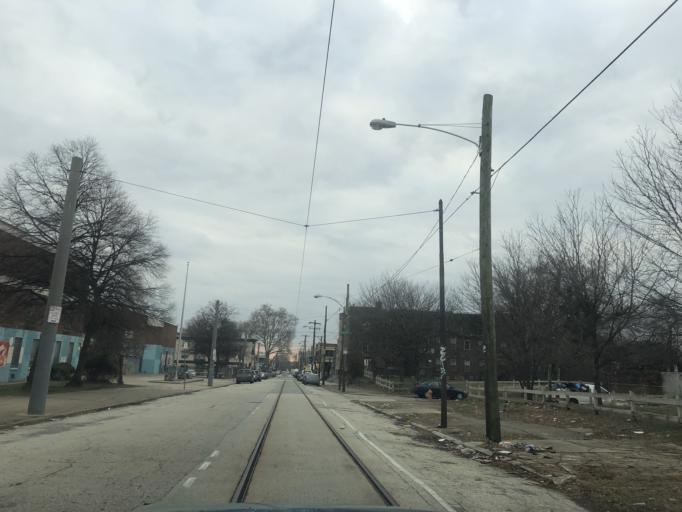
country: US
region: Pennsylvania
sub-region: Delaware County
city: Millbourne
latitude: 39.9784
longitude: -75.2302
